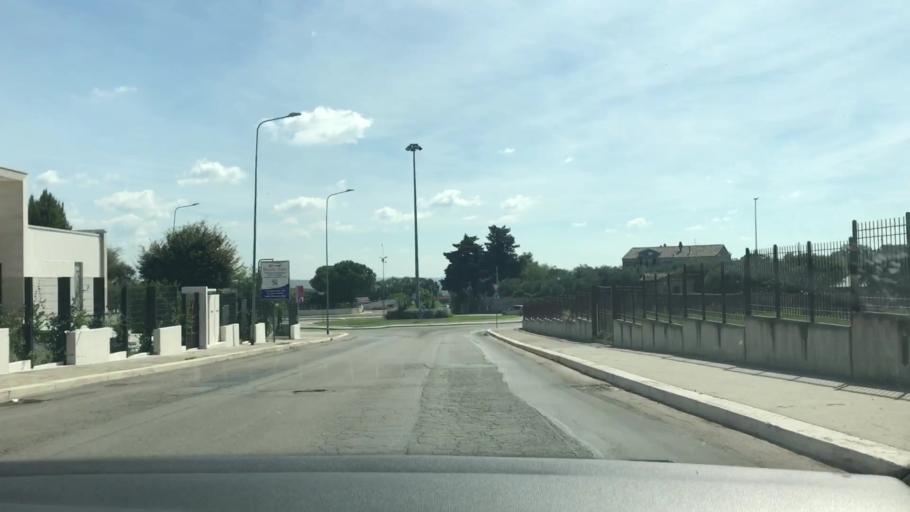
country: IT
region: Apulia
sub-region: Provincia di Bari
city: Altamura
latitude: 40.8256
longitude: 16.5656
